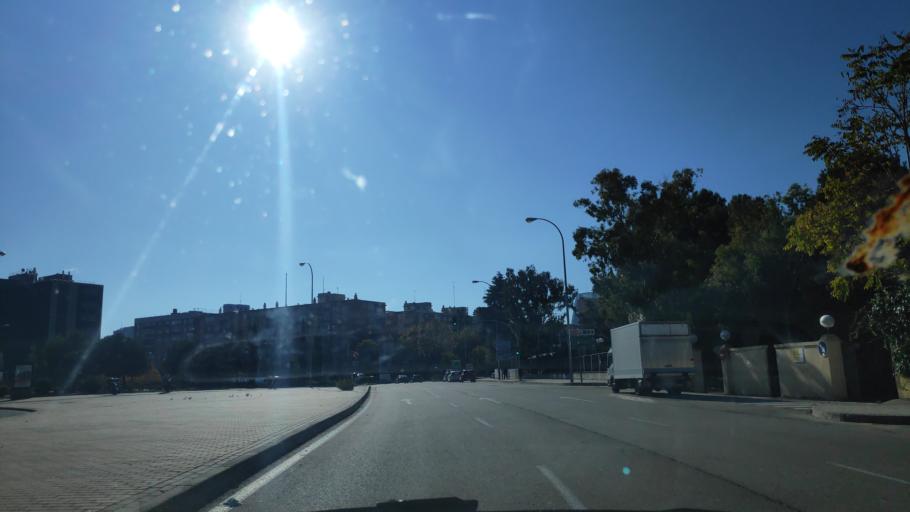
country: ES
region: Madrid
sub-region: Provincia de Madrid
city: Chamartin
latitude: 40.4758
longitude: -3.6900
